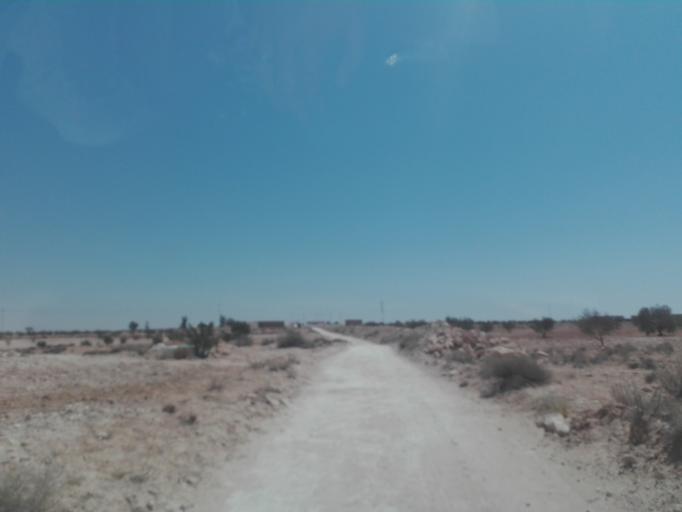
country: TN
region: Safaqis
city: Skhira
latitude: 34.4135
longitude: 9.9480
